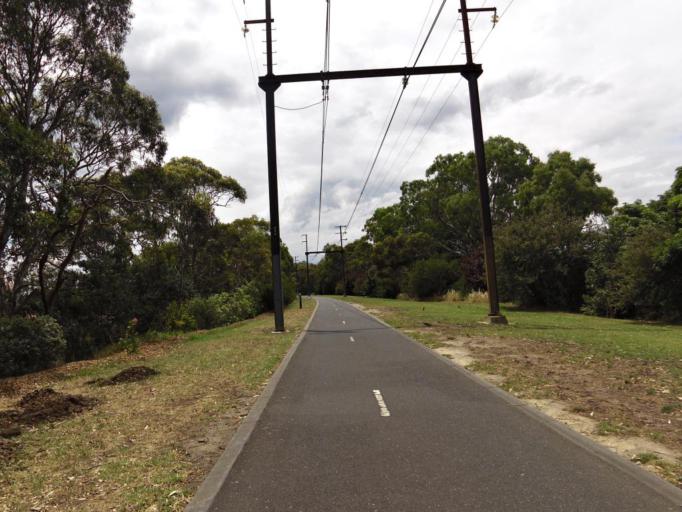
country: AU
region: Victoria
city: Ashburton
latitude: -37.8721
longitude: 145.0776
